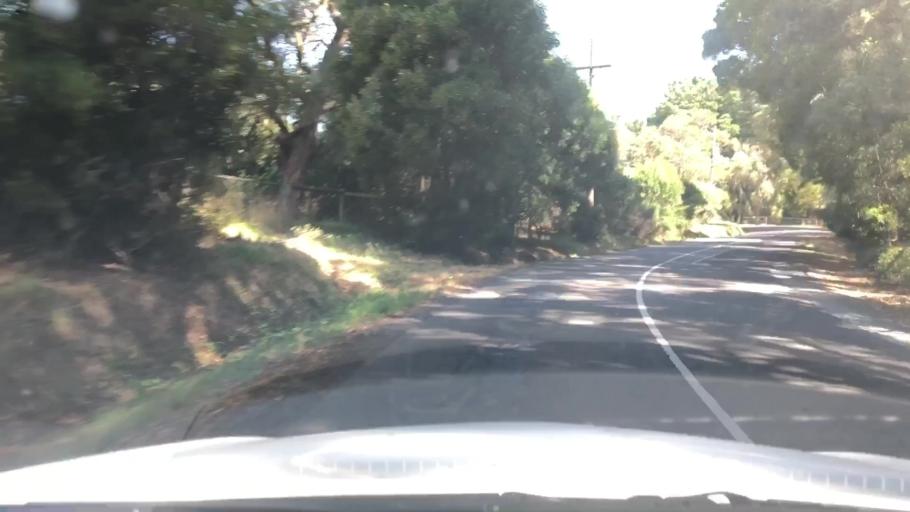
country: AU
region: Victoria
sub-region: Yarra Ranges
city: Macclesfield
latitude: -37.8993
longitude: 145.4698
